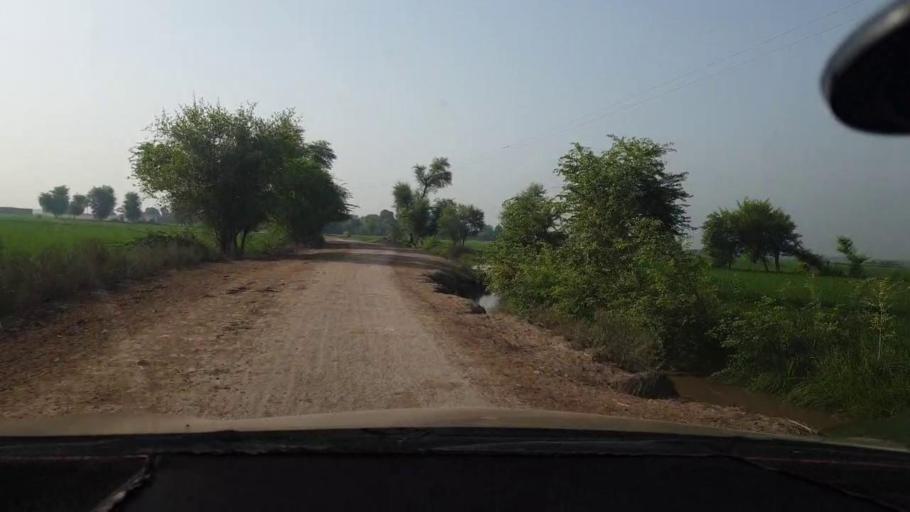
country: PK
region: Sindh
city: Kambar
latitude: 27.5377
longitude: 68.0182
